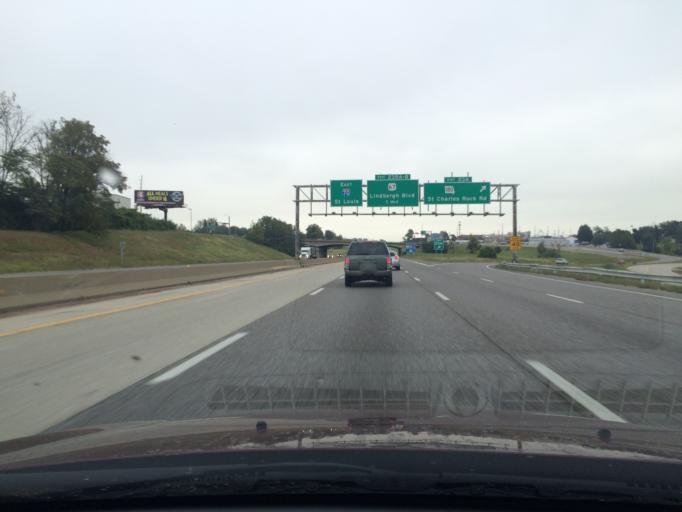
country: US
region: Missouri
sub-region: Saint Louis County
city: Bridgeton
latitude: 38.7436
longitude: -90.4166
